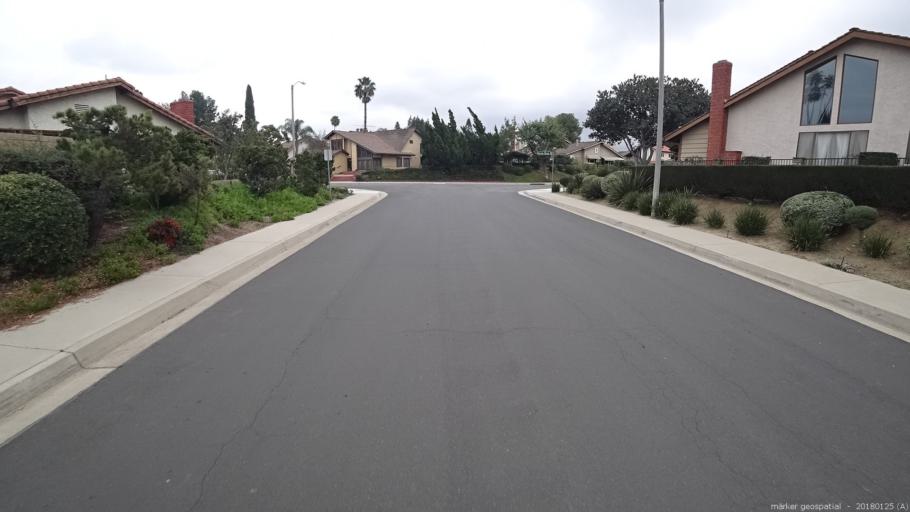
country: US
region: California
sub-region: Los Angeles County
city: Walnut
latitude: 33.9670
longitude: -117.8375
